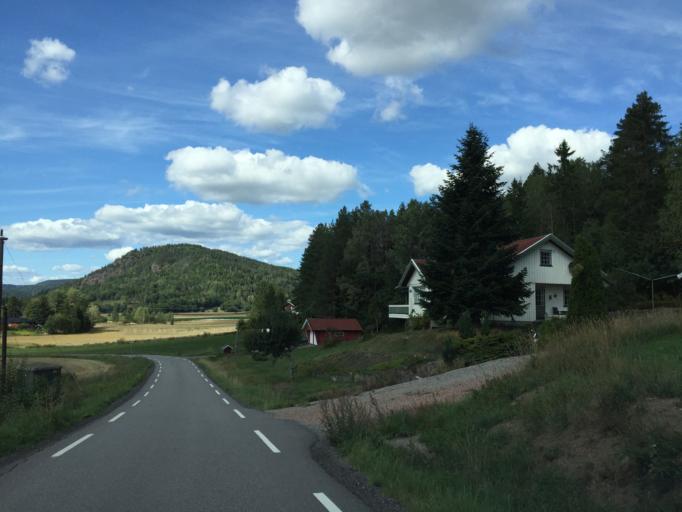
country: NO
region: Vestfold
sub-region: Hof
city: Hof
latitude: 59.4308
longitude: 10.1368
